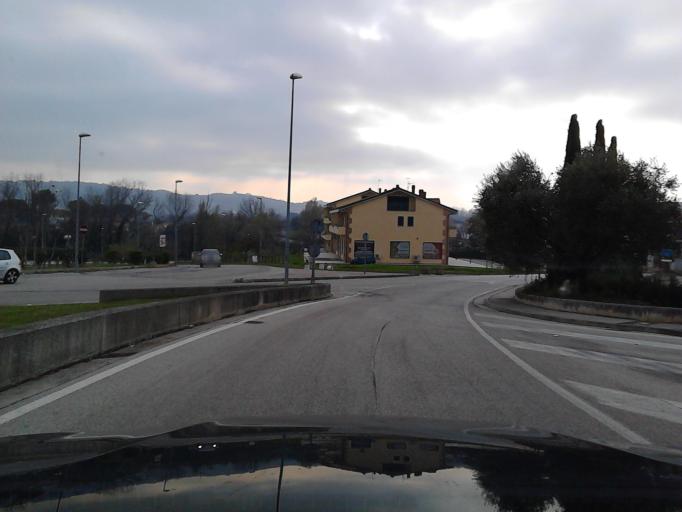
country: IT
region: Abruzzo
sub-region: Provincia di Teramo
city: Villa Rosa
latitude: 42.8364
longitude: 13.8948
